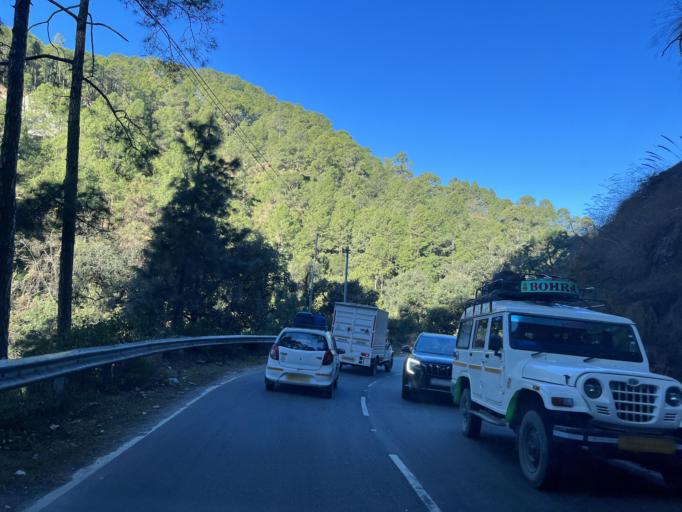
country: IN
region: Uttarakhand
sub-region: Naini Tal
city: Bhowali
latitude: 29.3944
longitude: 79.5115
